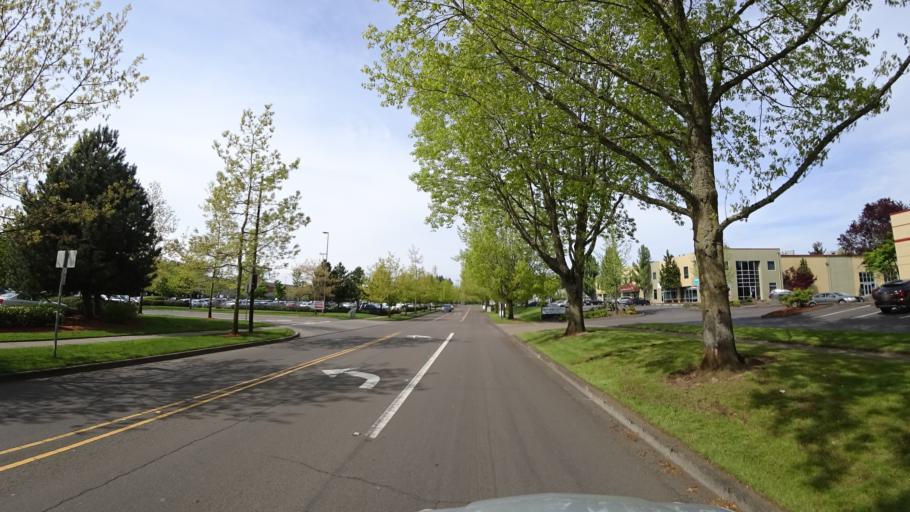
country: US
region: Oregon
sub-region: Washington County
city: Hillsboro
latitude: 45.5348
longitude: -122.9337
